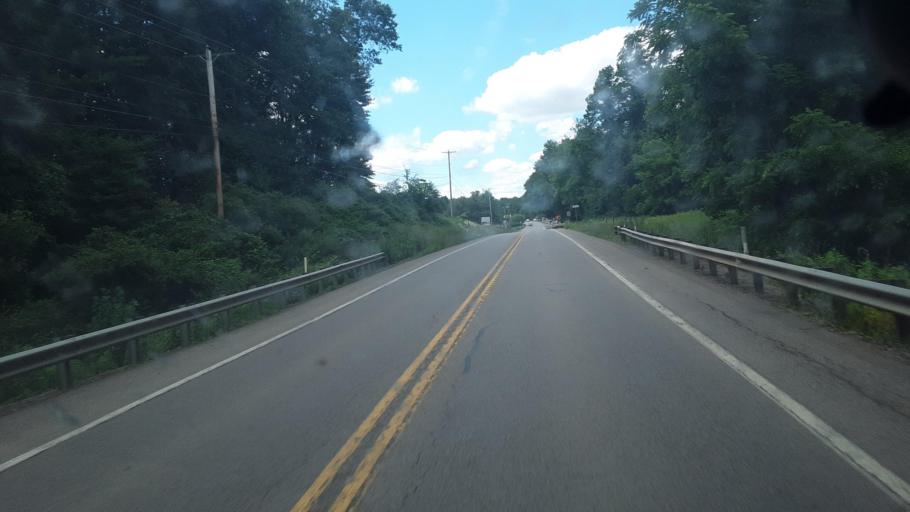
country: US
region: Pennsylvania
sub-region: Butler County
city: Slippery Rock
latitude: 41.0197
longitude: -80.1848
